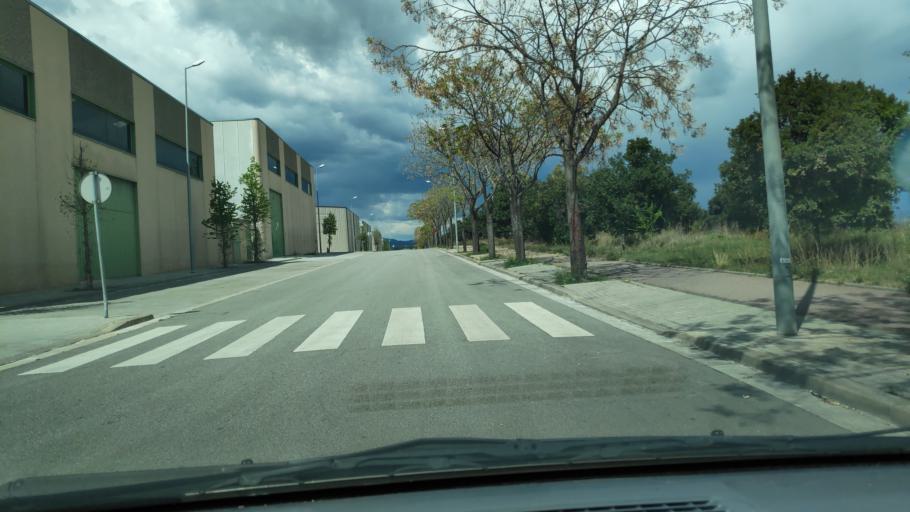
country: ES
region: Catalonia
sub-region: Provincia de Barcelona
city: Polinya
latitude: 41.5400
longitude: 2.1388
